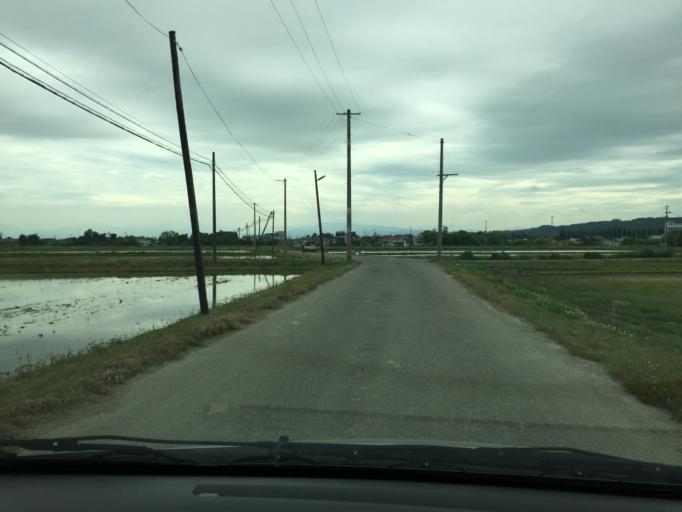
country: JP
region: Fukushima
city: Kitakata
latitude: 37.6830
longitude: 139.8751
